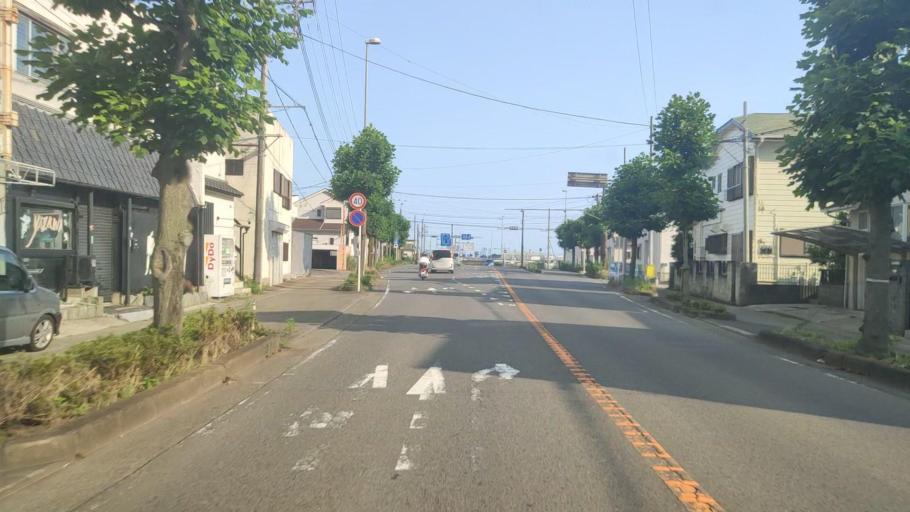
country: JP
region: Kanagawa
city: Isehara
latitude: 35.3764
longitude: 139.3192
